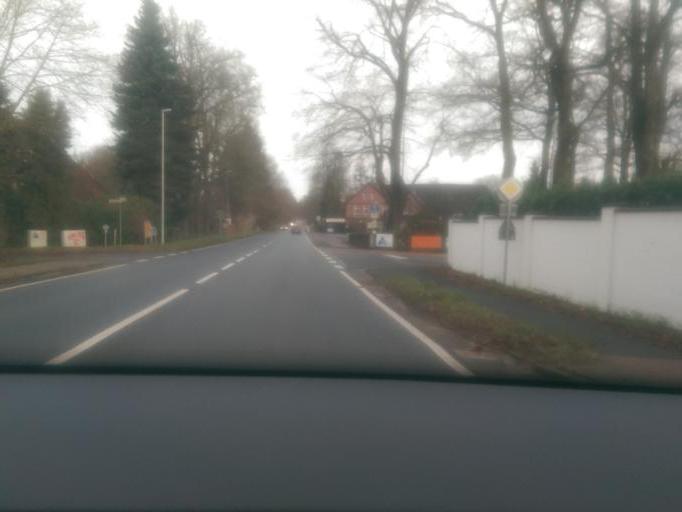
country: DE
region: Lower Saxony
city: Elze
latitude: 52.5634
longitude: 9.7252
